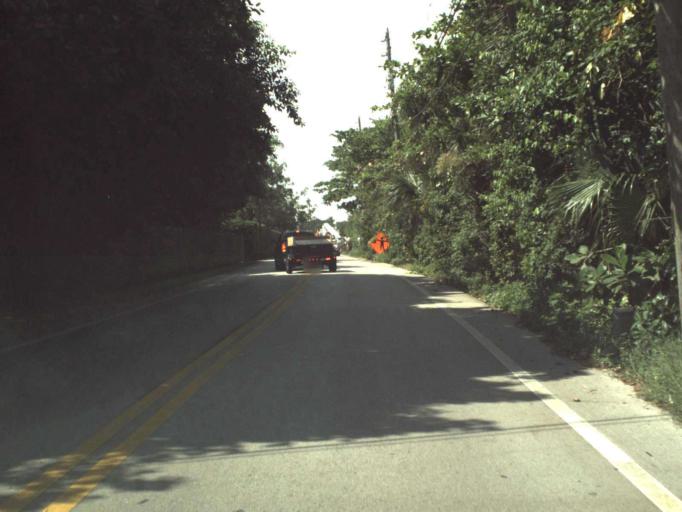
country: US
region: Florida
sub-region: Palm Beach County
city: Palm Beach
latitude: 26.6735
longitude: -80.0381
